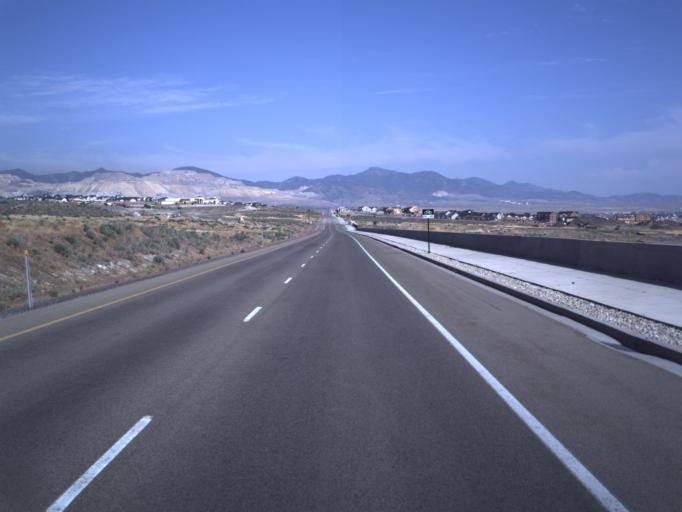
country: US
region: Utah
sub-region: Salt Lake County
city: Bluffdale
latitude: 40.4785
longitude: -111.9817
